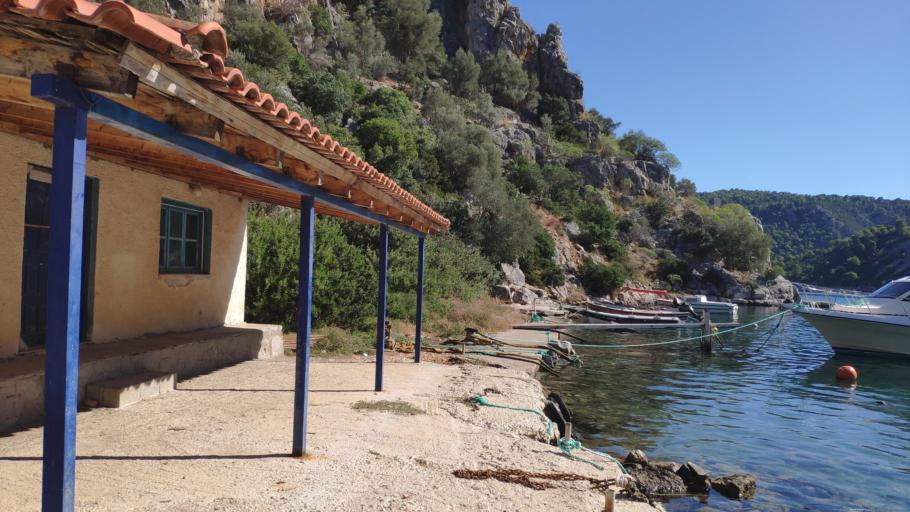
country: GR
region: Peloponnese
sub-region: Nomos Korinthias
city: Sofikon
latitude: 37.7334
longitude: 23.1191
